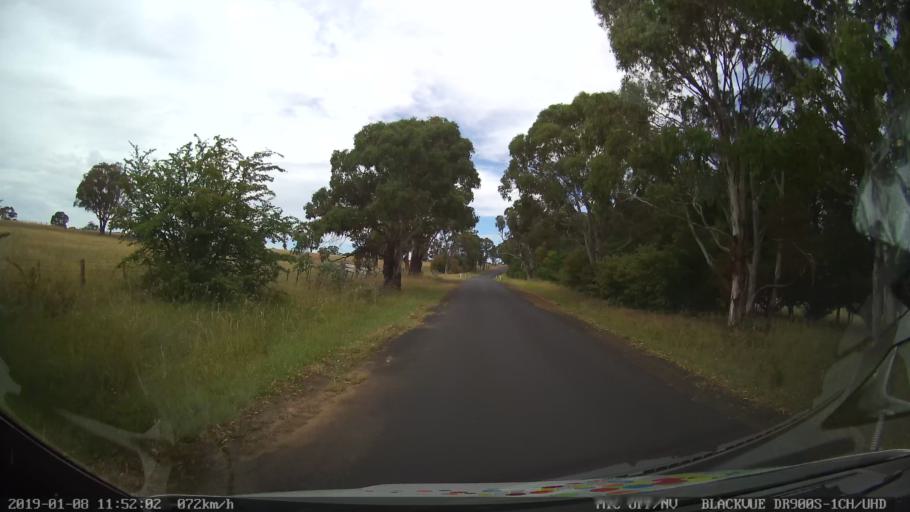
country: AU
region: New South Wales
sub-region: Armidale Dumaresq
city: Armidale
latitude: -30.3995
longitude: 151.5610
